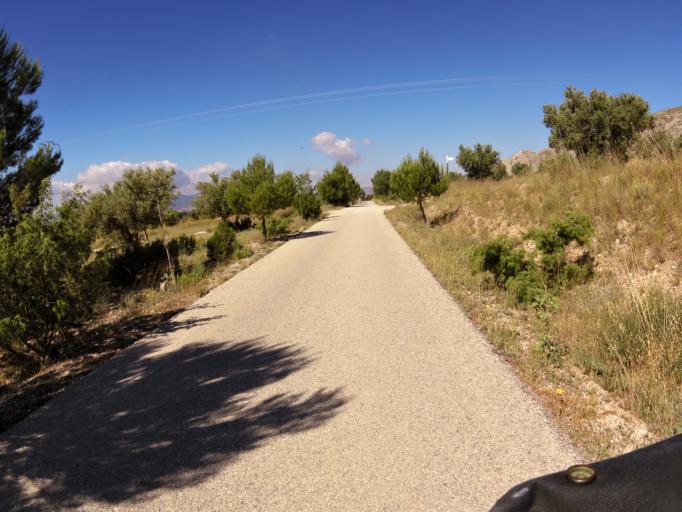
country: ES
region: Valencia
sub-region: Provincia de Alicante
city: Villena
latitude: 38.6371
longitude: -0.8296
